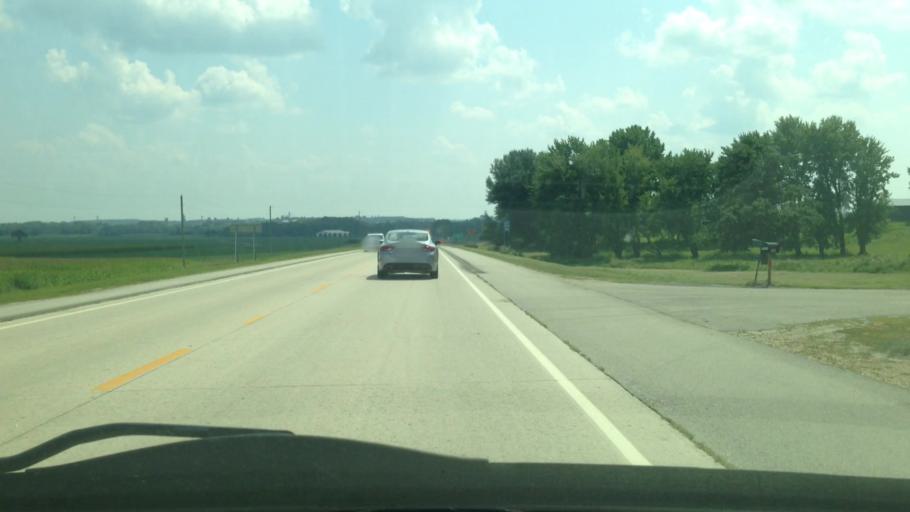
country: US
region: Minnesota
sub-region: Fillmore County
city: Spring Valley
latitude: 43.5123
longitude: -92.3694
